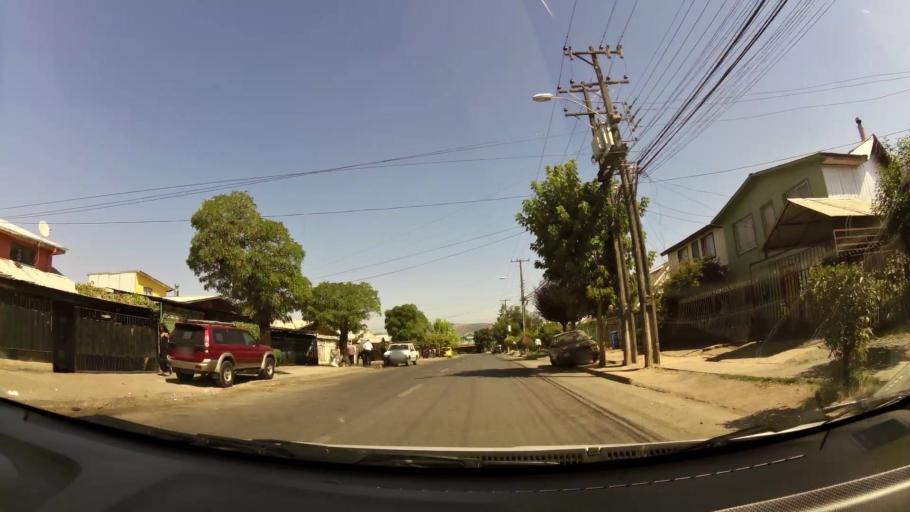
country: CL
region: Maule
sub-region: Provincia de Talca
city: Talca
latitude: -35.4220
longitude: -71.6438
